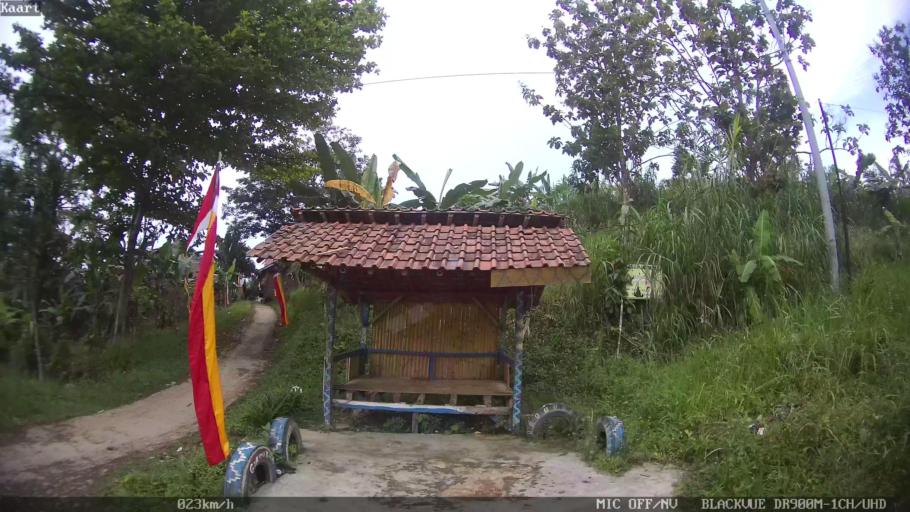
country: ID
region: Lampung
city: Kedaton
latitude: -5.3975
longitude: 105.1919
